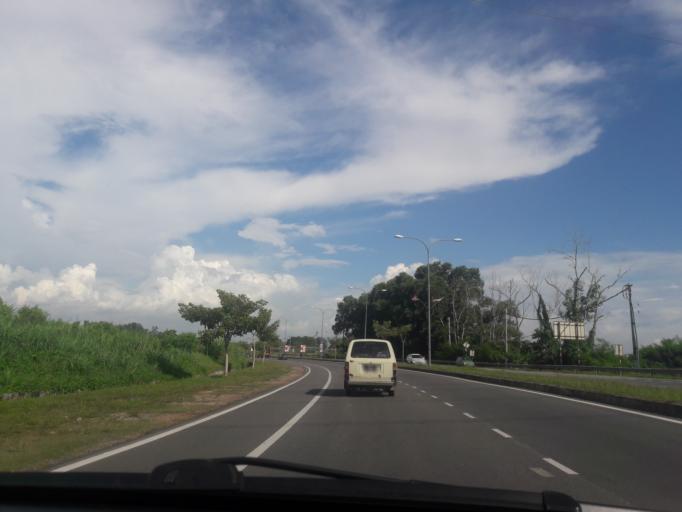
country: MY
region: Kedah
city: Sungai Petani
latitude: 5.6167
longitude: 100.4674
